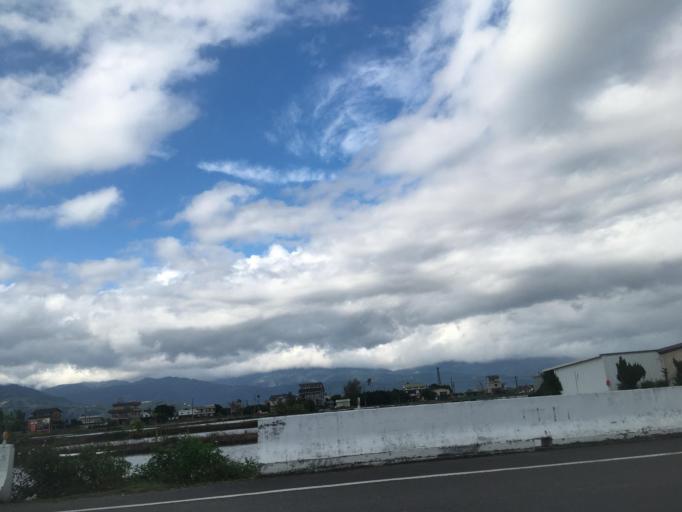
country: TW
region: Taiwan
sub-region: Yilan
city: Yilan
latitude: 24.6909
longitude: 121.7262
